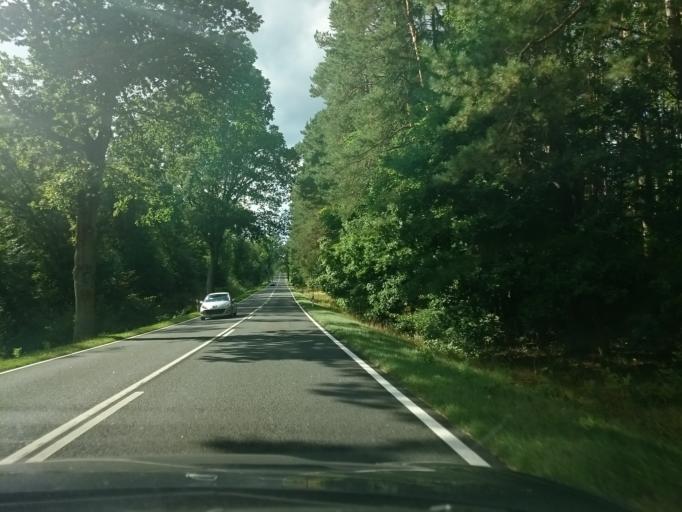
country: DE
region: Mecklenburg-Vorpommern
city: Carpin
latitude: 53.3657
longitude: 13.2027
